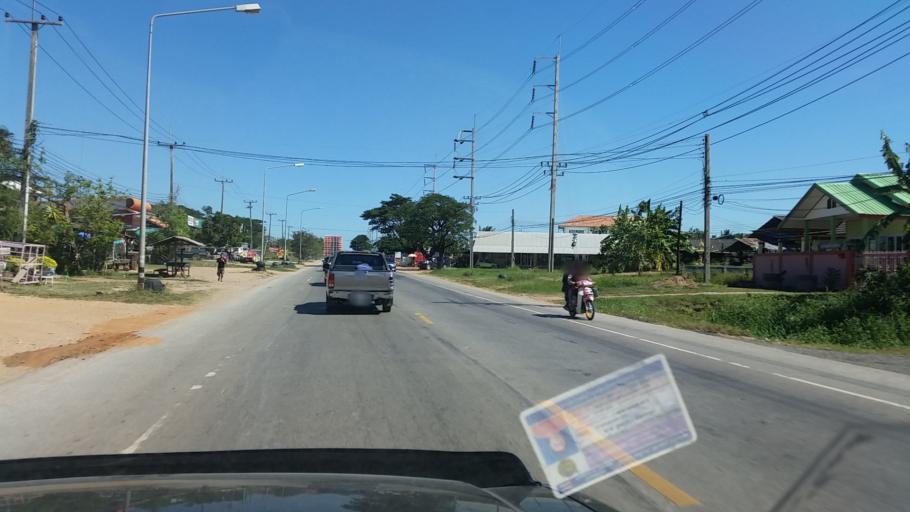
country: TH
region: Chaiyaphum
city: Ban Khwao
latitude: 15.7810
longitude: 101.8983
